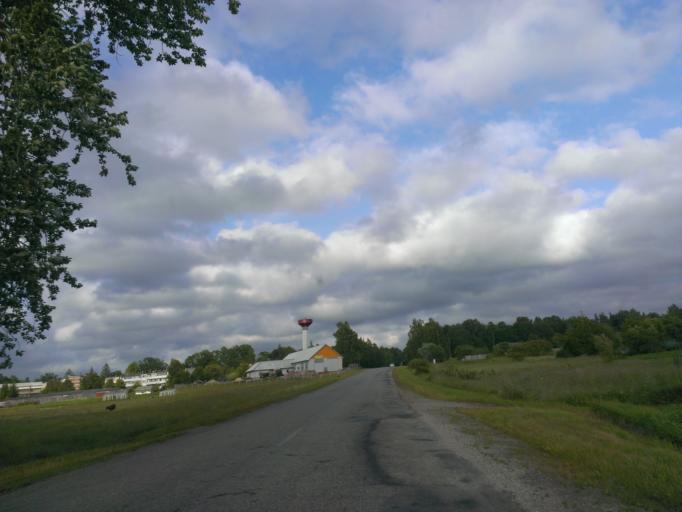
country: LV
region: Aizpute
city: Aizpute
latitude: 56.7310
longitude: 21.7224
